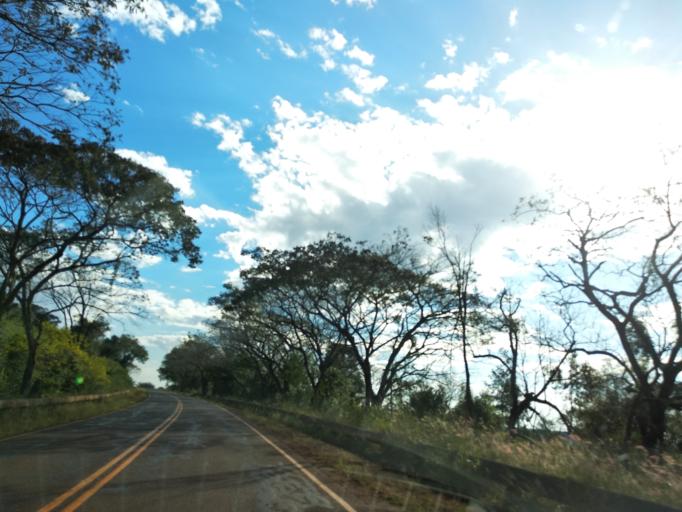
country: AR
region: Misiones
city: Jardin America
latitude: -27.0365
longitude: -55.2028
